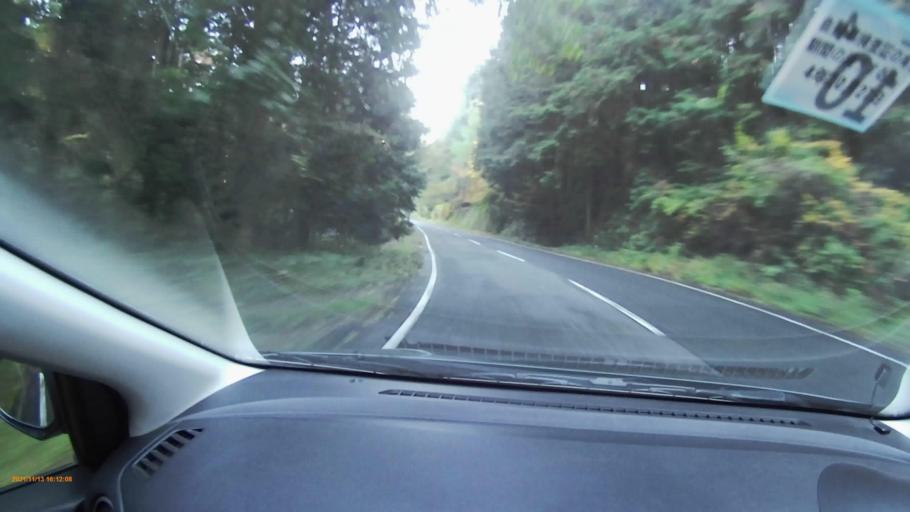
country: JP
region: Gifu
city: Nakatsugawa
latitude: 35.5836
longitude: 137.5093
